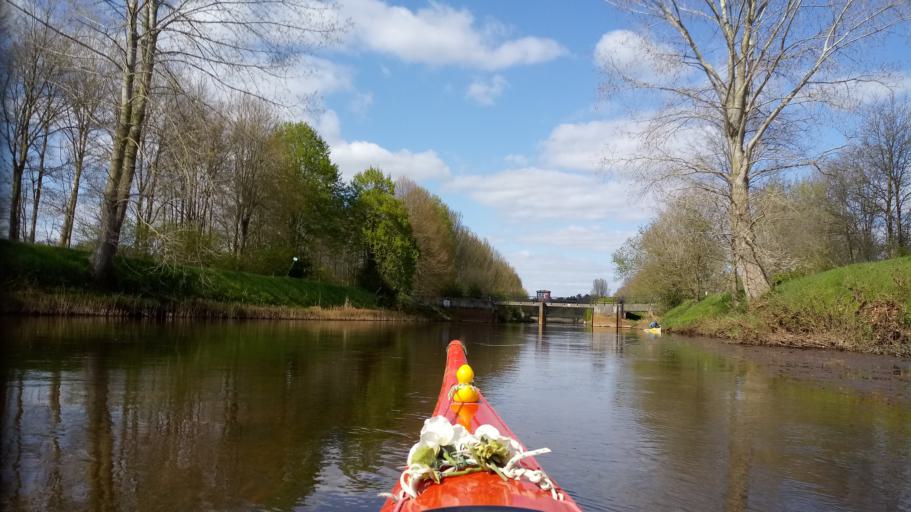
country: NL
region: Overijssel
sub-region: Gemeente Twenterand
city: Den Ham
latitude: 52.4684
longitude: 6.4522
